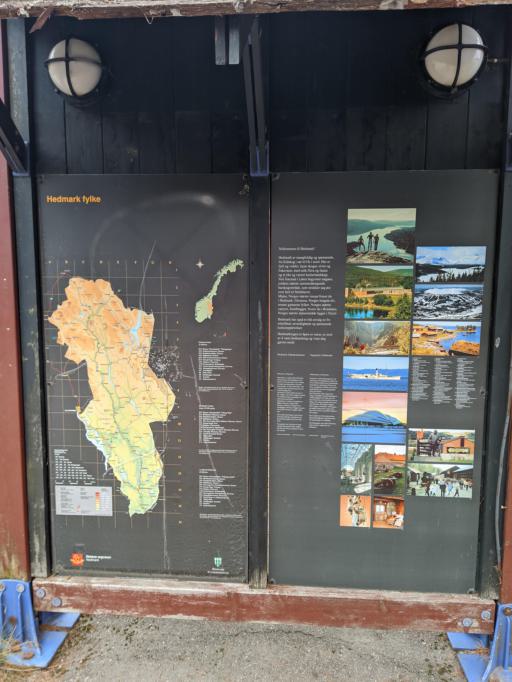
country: NO
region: Hedmark
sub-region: Amot
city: Rena
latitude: 61.1643
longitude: 11.4617
